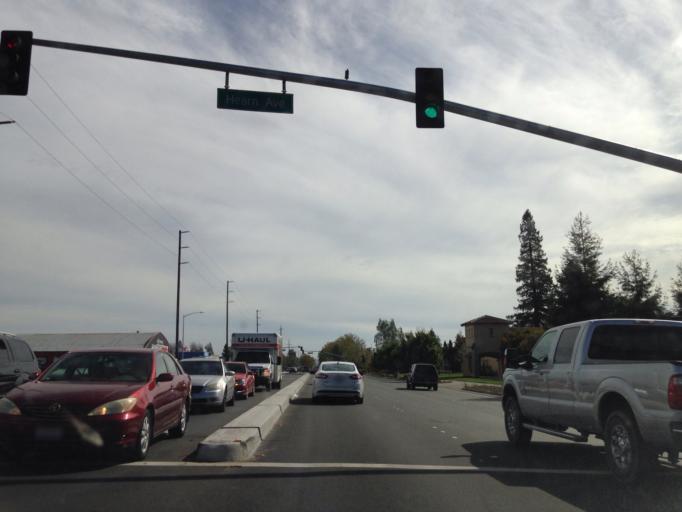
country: US
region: California
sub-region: Sonoma County
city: Roseland
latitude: 38.4151
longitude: -122.7136
